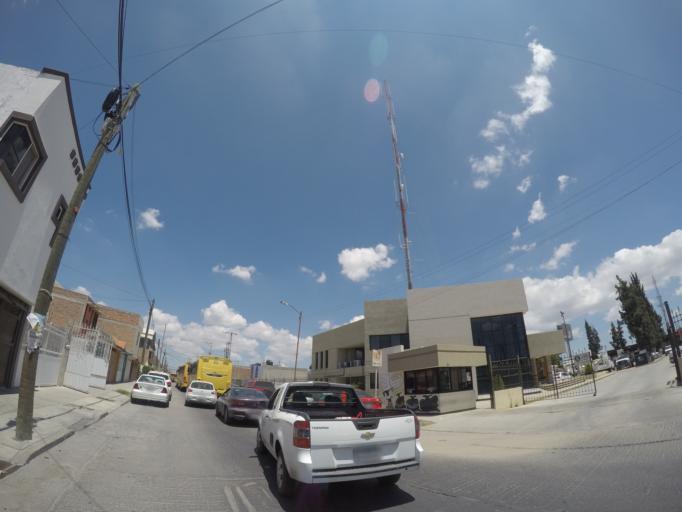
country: MX
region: San Luis Potosi
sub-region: San Luis Potosi
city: San Luis Potosi
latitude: 22.1538
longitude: -100.9585
